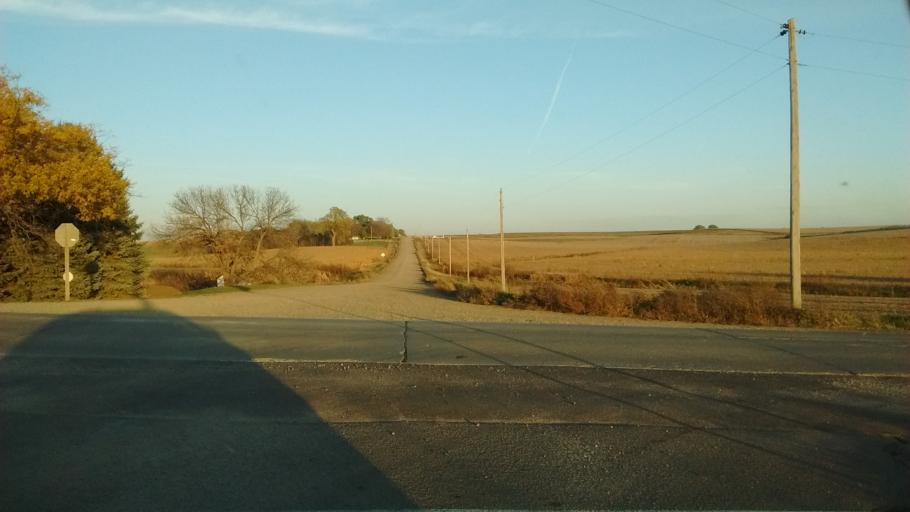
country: US
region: Iowa
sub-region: Plymouth County
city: Le Mars
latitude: 42.7642
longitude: -96.1557
